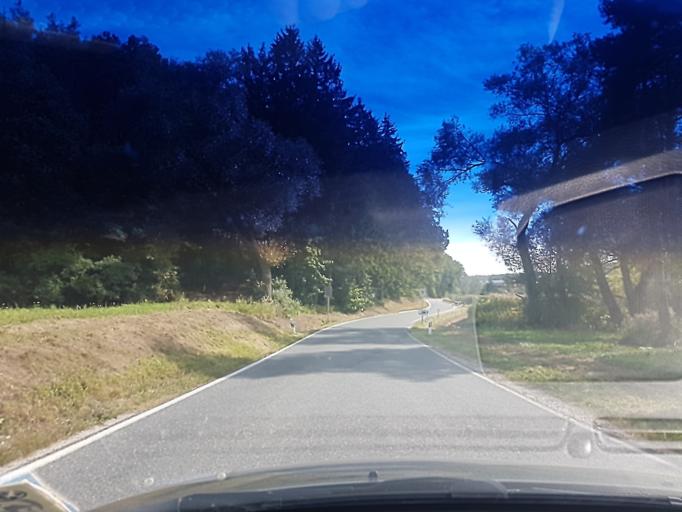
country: DE
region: Bavaria
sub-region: Regierungsbezirk Mittelfranken
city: Wachenroth
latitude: 49.7774
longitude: 10.7109
